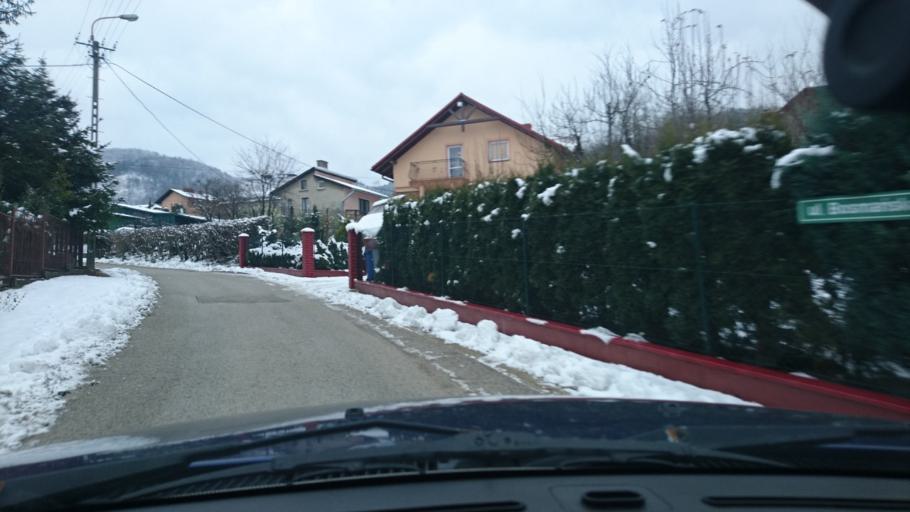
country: PL
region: Silesian Voivodeship
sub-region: Powiat bielski
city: Kozy
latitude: 49.8208
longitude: 19.1203
